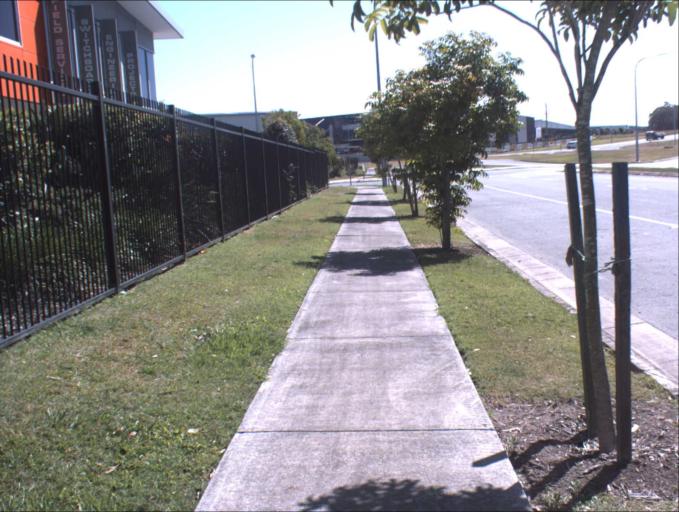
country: AU
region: Queensland
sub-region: Logan
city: Woodridge
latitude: -27.6533
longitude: 153.0755
